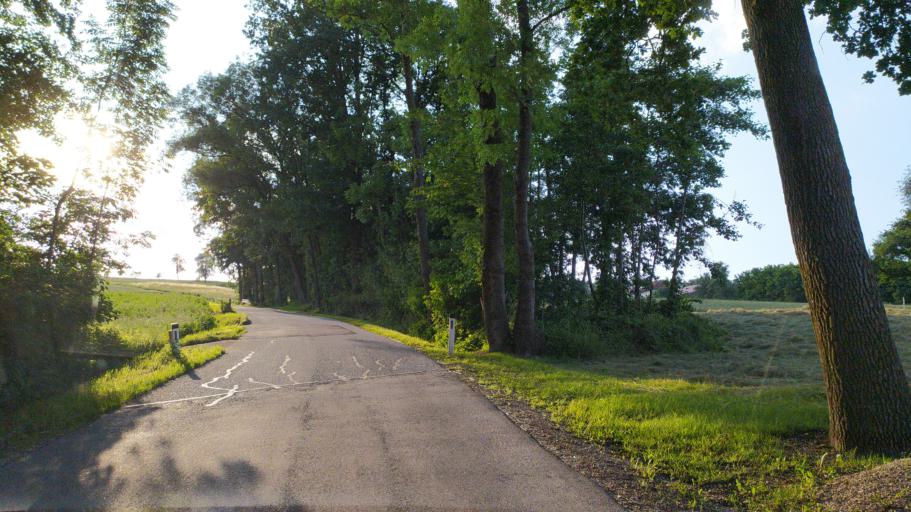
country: AT
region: Lower Austria
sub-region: Politischer Bezirk Amstetten
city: Strengberg
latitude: 48.1506
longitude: 14.6801
